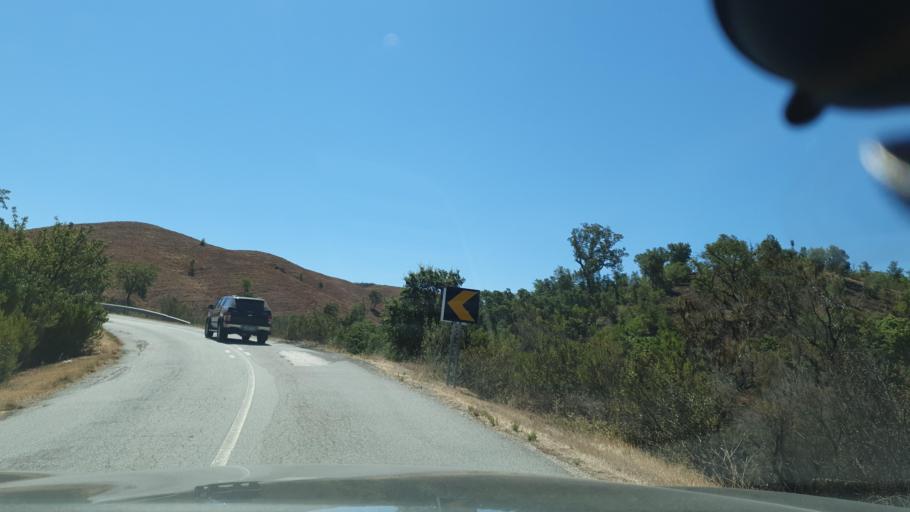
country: PT
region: Faro
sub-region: Monchique
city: Monchique
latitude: 37.4199
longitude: -8.5460
